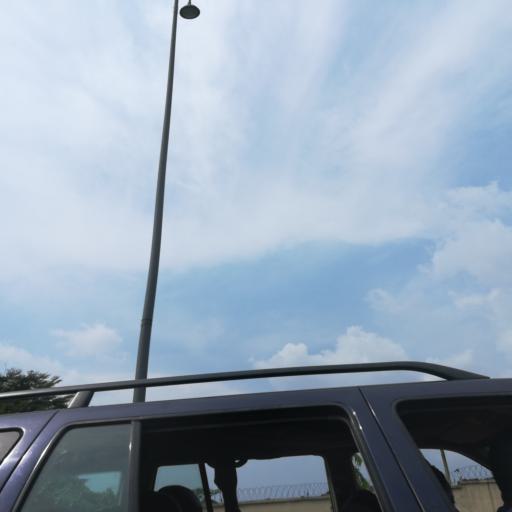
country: NG
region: Rivers
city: Port Harcourt
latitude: 4.8518
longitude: 7.0175
